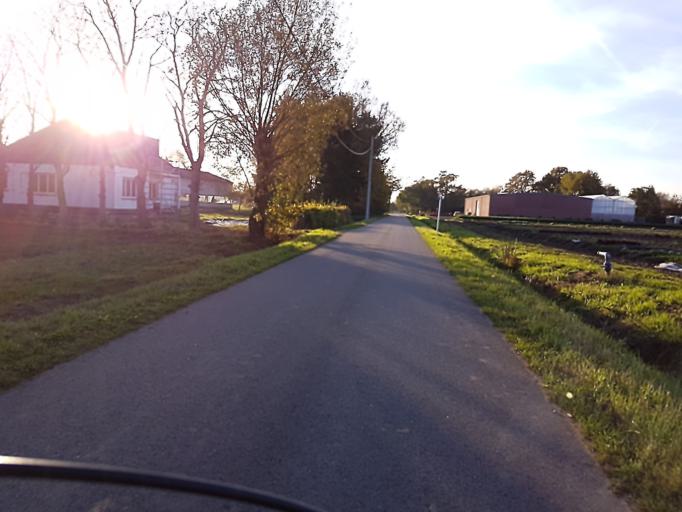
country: BE
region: Flanders
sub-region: Provincie Antwerpen
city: Bonheiden
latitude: 51.0467
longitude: 4.5864
